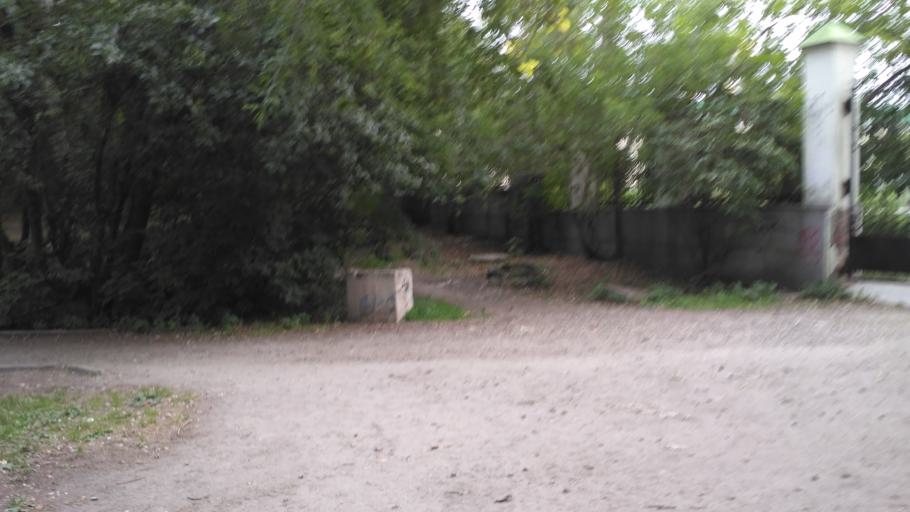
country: RU
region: Sverdlovsk
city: Yekaterinburg
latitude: 56.8467
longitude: 60.6114
